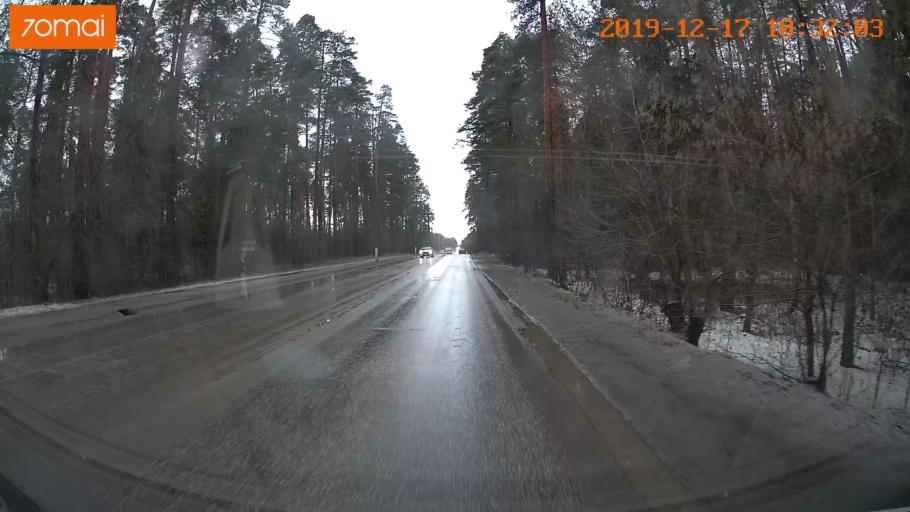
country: RU
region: Vladimir
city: Gus'-Khrustal'nyy
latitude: 55.6314
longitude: 40.6923
